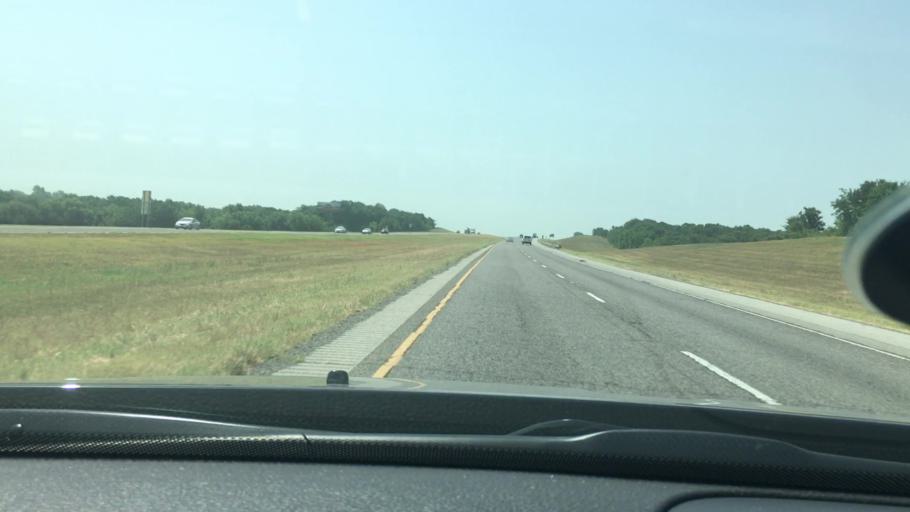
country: US
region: Oklahoma
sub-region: Garvin County
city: Wynnewood
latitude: 34.5833
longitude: -97.2032
